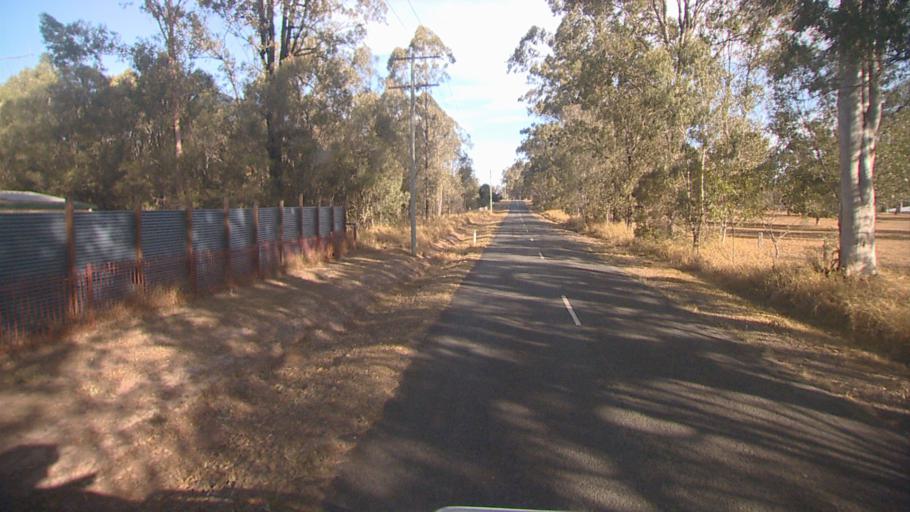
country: AU
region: Queensland
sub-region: Logan
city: Cedar Vale
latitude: -27.8699
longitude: 153.0110
